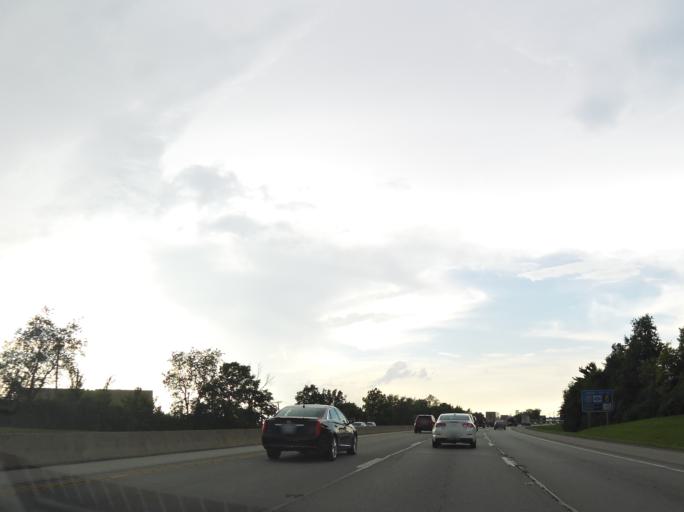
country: US
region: Kentucky
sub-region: Fayette County
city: Lexington-Fayette
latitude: 38.0296
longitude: -84.4185
